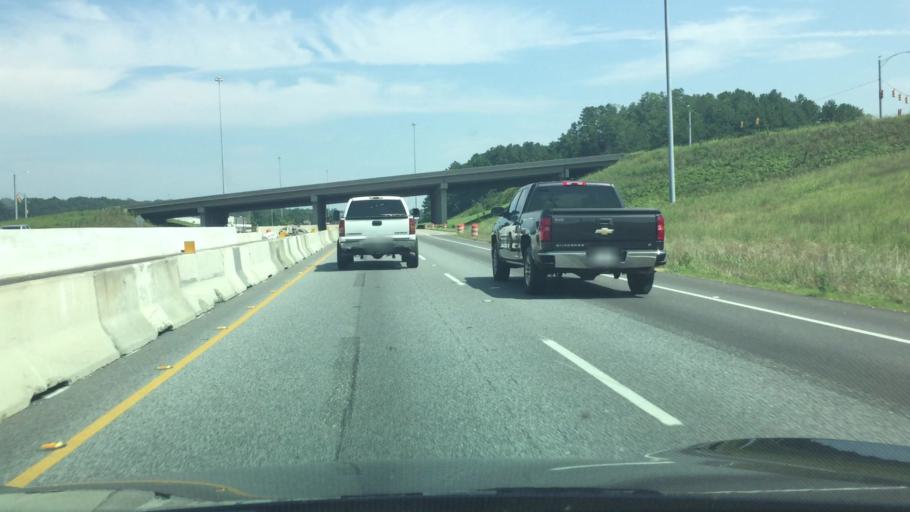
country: US
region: Alabama
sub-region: Shelby County
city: Pelham
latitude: 33.2785
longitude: -86.7998
